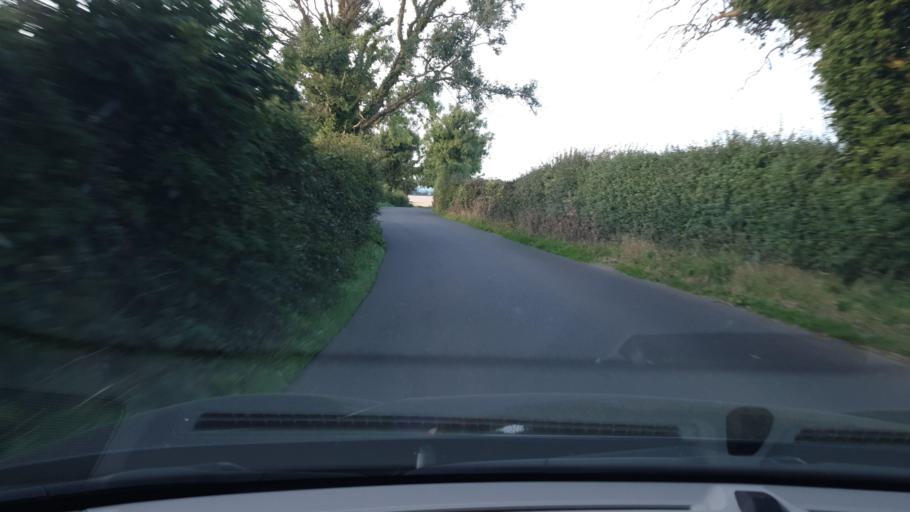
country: IE
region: Leinster
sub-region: An Mhi
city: Ashbourne
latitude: 53.5394
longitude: -6.3334
